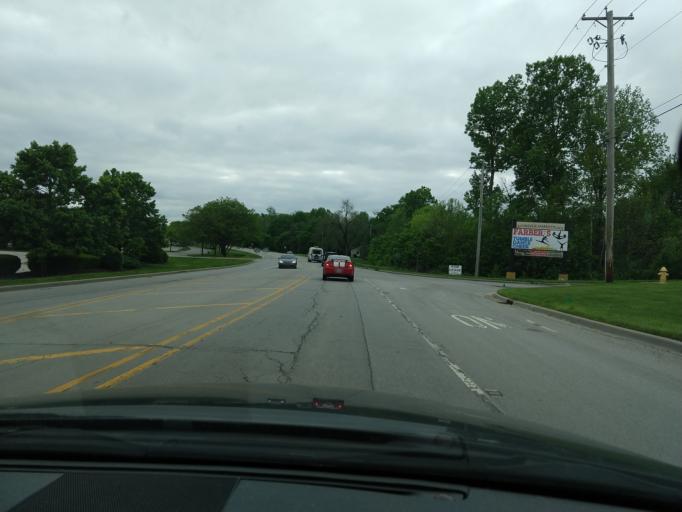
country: US
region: Indiana
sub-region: Hamilton County
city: Noblesville
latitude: 40.0470
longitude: -86.0296
